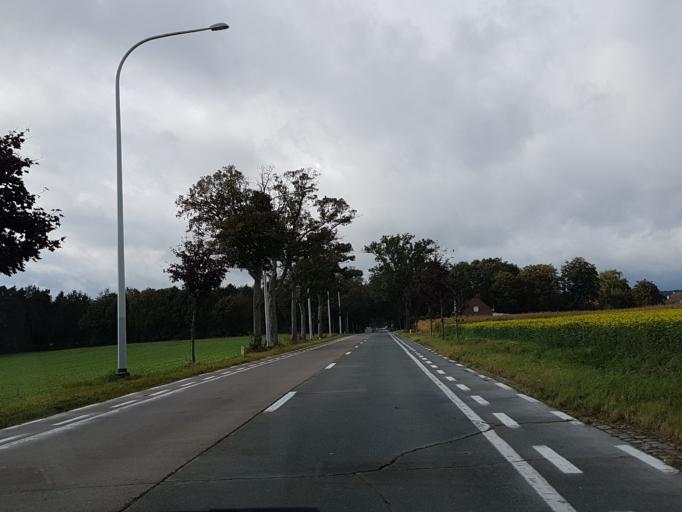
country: BE
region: Flanders
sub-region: Provincie Vlaams-Brabant
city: Boutersem
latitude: 50.8513
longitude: 4.8083
